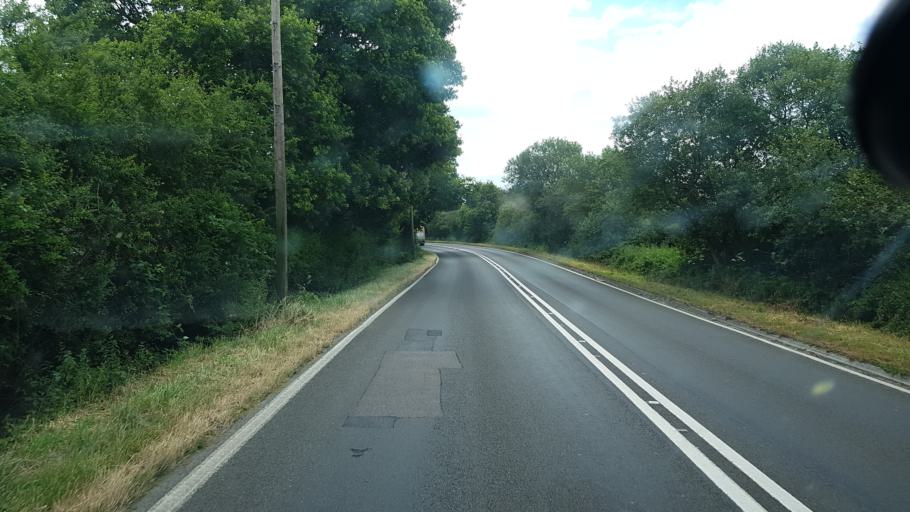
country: GB
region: England
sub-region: Surrey
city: Felbridge
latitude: 51.1710
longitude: -0.0501
